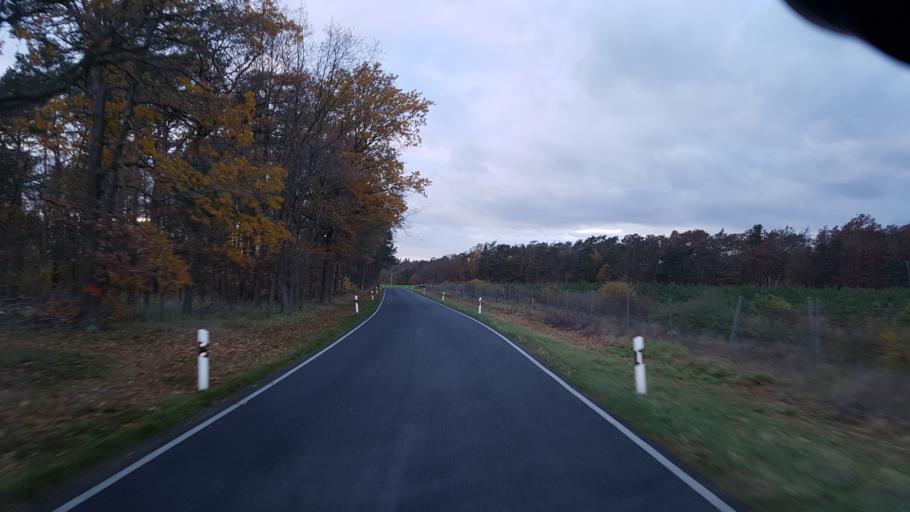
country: DE
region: Brandenburg
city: Tettau
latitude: 51.4243
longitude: 13.7441
